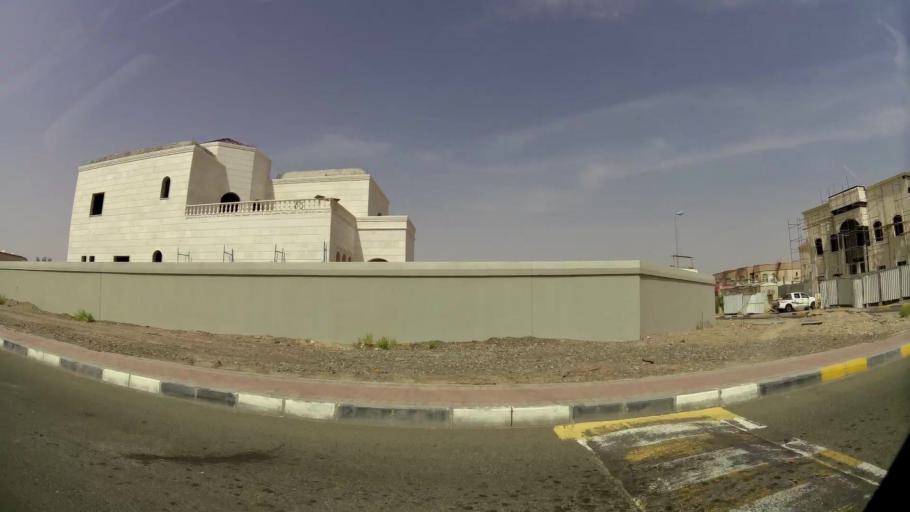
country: AE
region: Abu Dhabi
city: Al Ain
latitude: 24.1701
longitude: 55.6759
